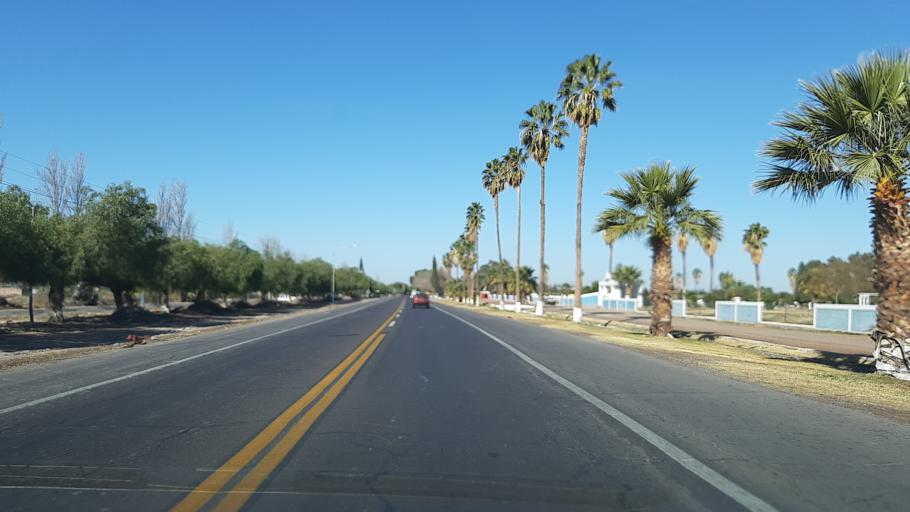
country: AR
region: San Juan
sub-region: Departamento de Santa Lucia
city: Santa Lucia
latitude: -31.5706
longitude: -68.4414
